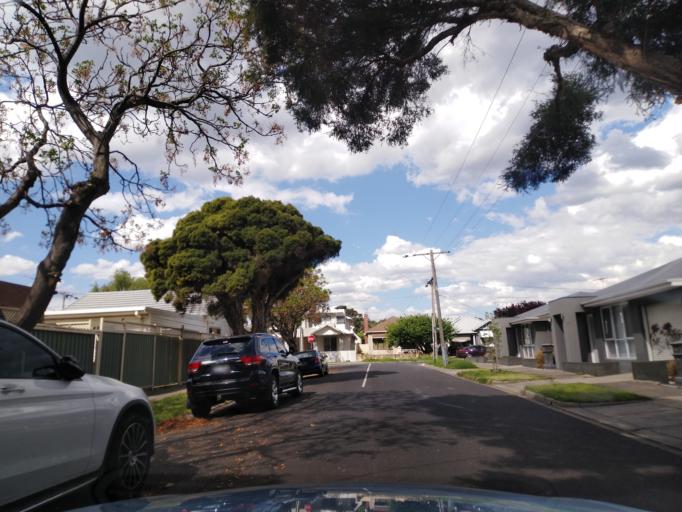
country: AU
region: Victoria
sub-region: Hobsons Bay
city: Newport
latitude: -37.8429
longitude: 144.8792
